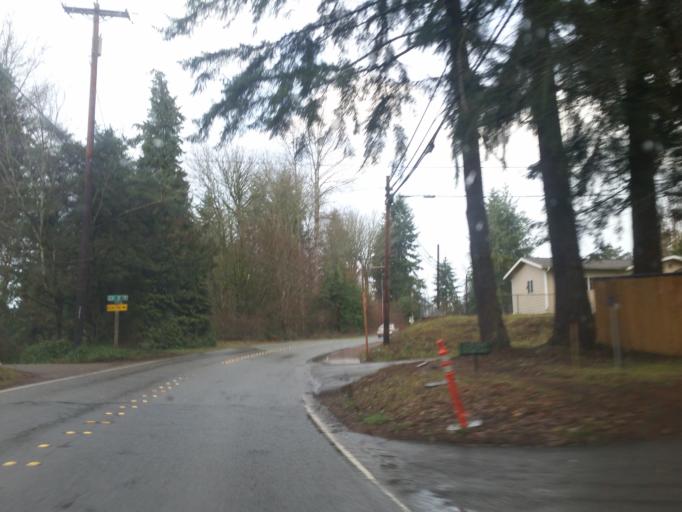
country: US
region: Washington
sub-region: Snohomish County
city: Brier
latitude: 47.7888
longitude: -122.2562
